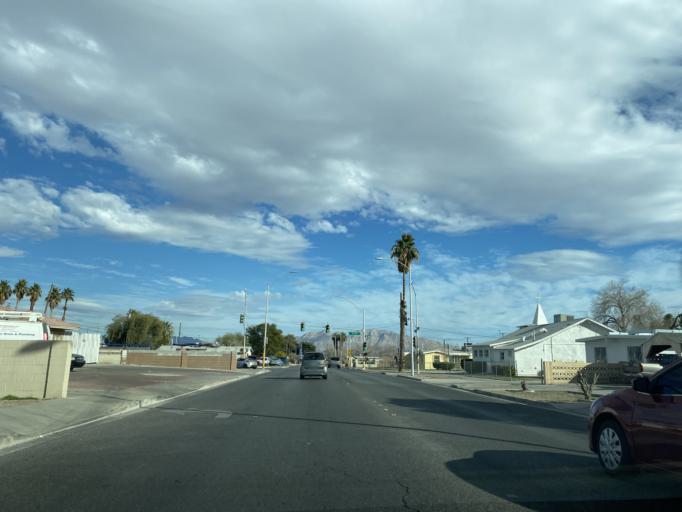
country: US
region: Nevada
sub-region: Clark County
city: Las Vegas
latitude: 36.1880
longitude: -115.1480
